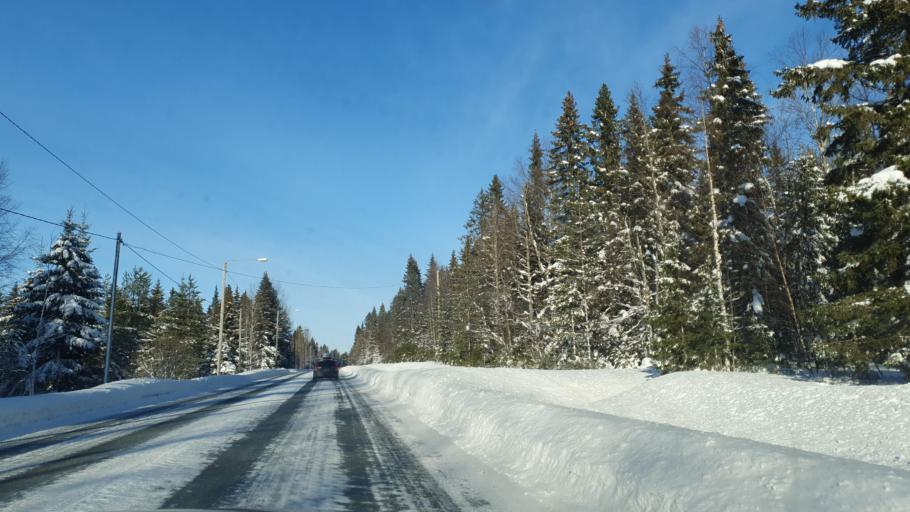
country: FI
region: Lapland
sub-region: Kemi-Tornio
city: Tornio
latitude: 65.9998
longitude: 24.0725
